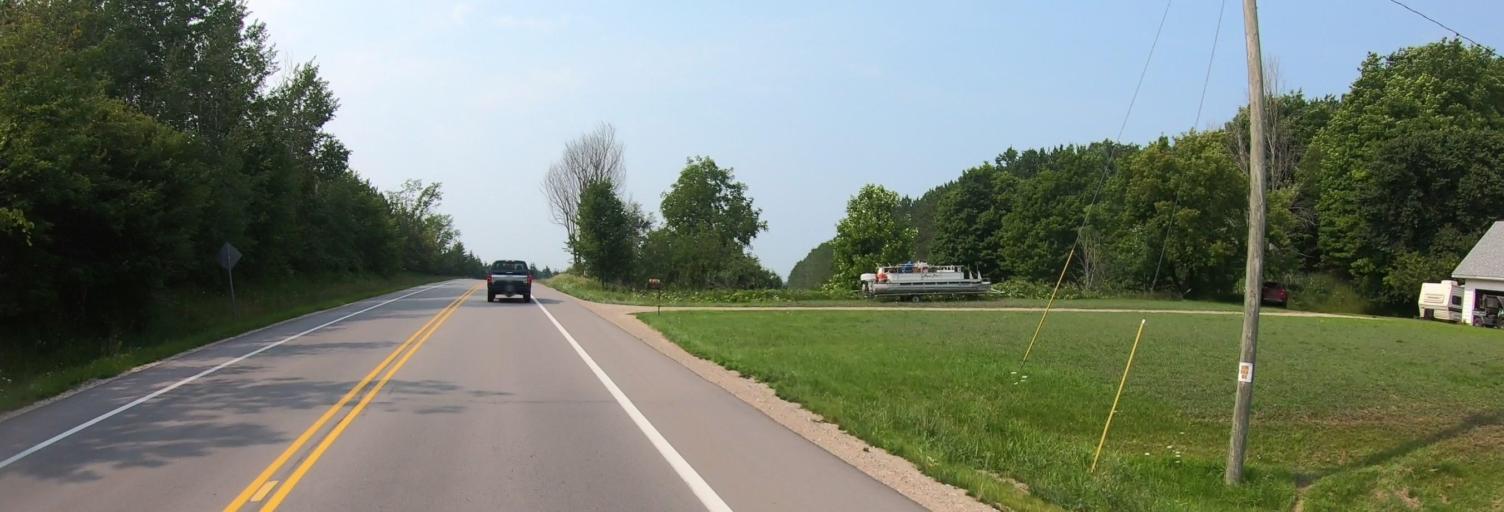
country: US
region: Michigan
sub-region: Charlevoix County
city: Charlevoix
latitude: 45.2572
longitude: -85.2627
